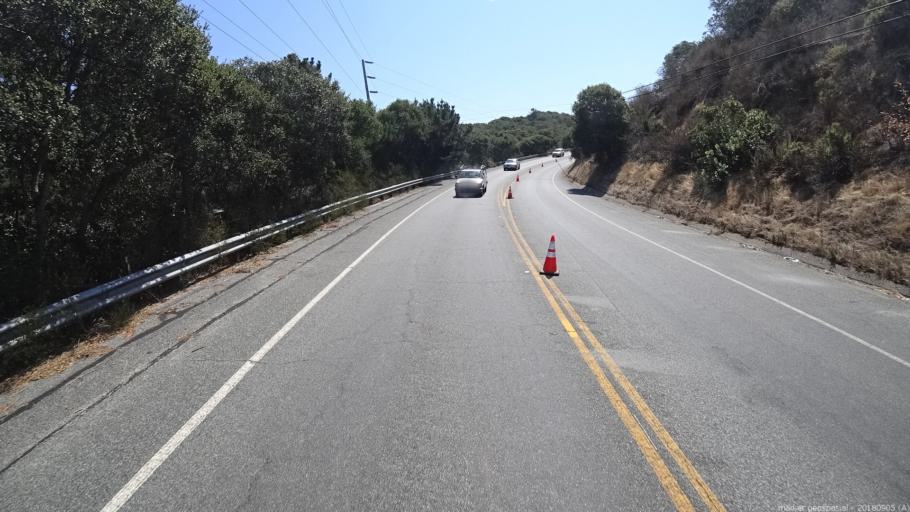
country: US
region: California
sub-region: Monterey County
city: Carmel Valley Village
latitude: 36.5629
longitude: -121.7499
